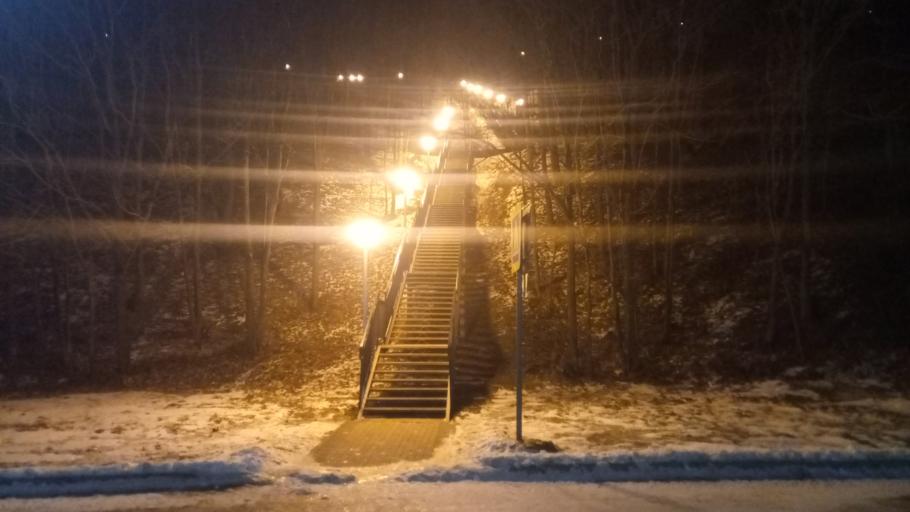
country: RU
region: Chuvashia
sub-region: Cheboksarskiy Rayon
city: Cheboksary
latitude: 56.1556
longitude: 47.1969
